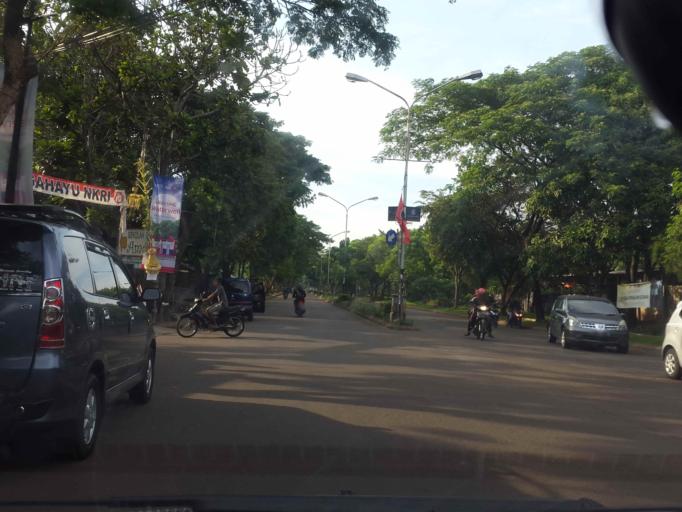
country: ID
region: Banten
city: South Tangerang
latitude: -6.2731
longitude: 106.6928
